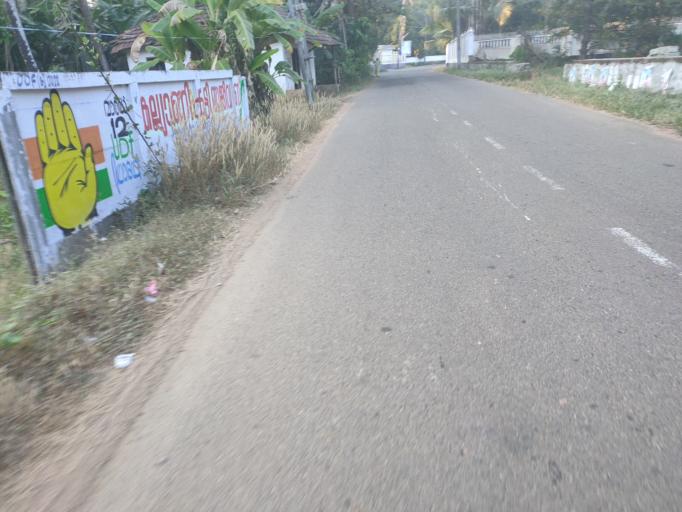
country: IN
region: Kerala
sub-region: Ernakulam
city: Angamali
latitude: 10.2194
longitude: 76.3285
